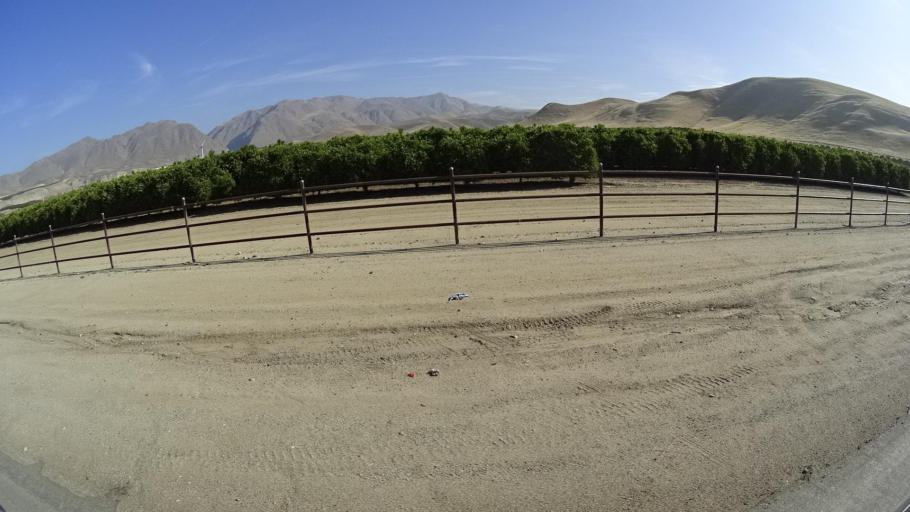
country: US
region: California
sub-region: Kern County
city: Lamont
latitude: 35.4189
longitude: -118.8315
